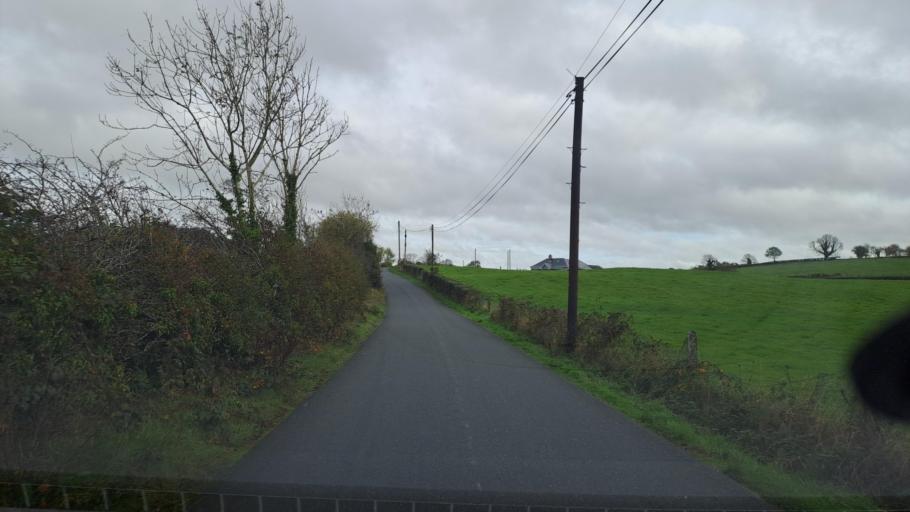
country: IE
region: Ulster
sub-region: An Cabhan
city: Bailieborough
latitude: 54.0125
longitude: -6.8884
